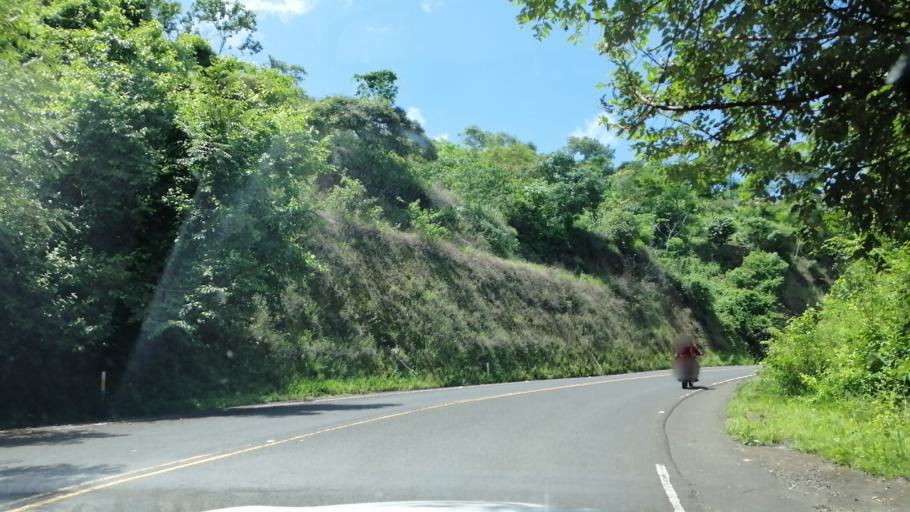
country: SV
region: San Miguel
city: Ciudad Barrios
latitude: 13.7952
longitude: -88.2912
